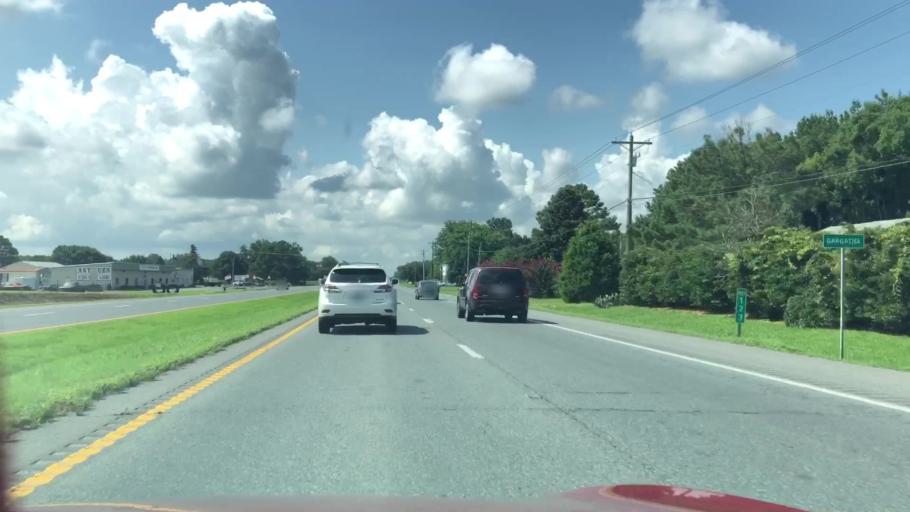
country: US
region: Virginia
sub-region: Accomack County
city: Accomac
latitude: 37.8027
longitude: -75.5975
